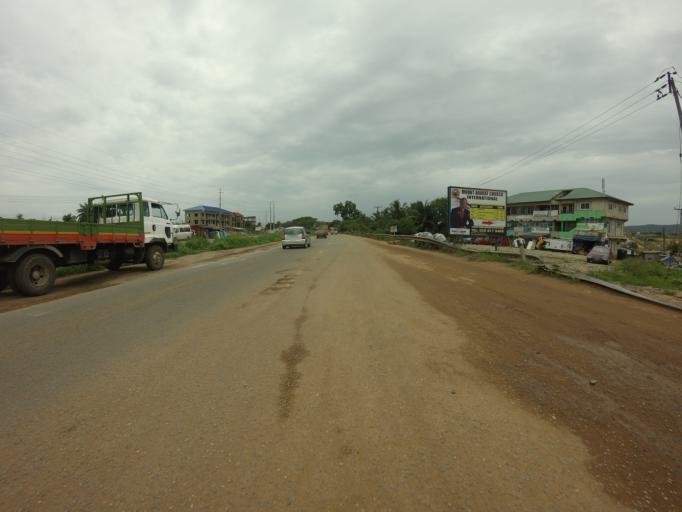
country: GH
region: Greater Accra
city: Achiaman
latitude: 5.7072
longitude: -0.2991
